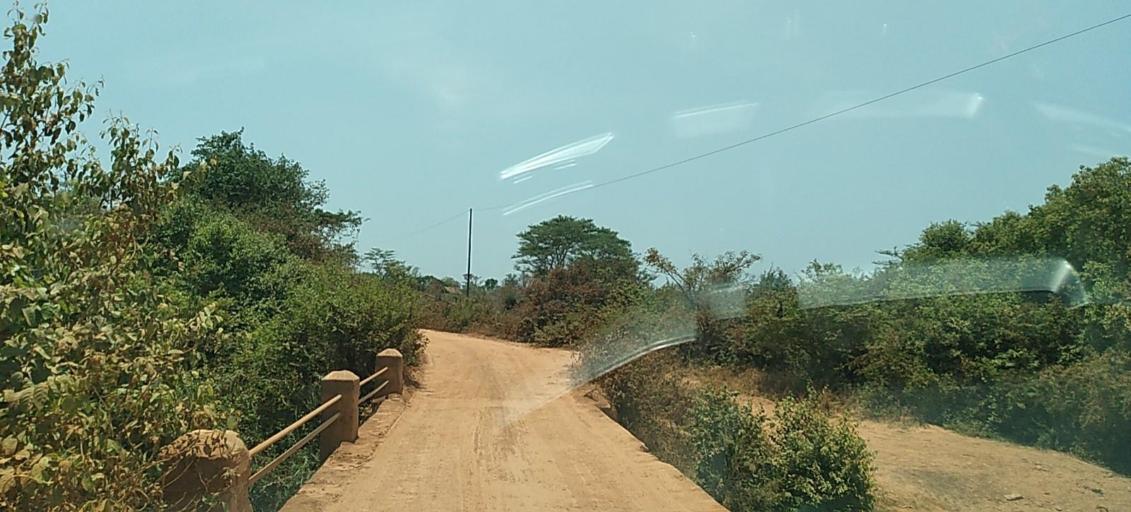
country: CD
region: Katanga
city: Kipushi
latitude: -11.7878
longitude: 27.1684
